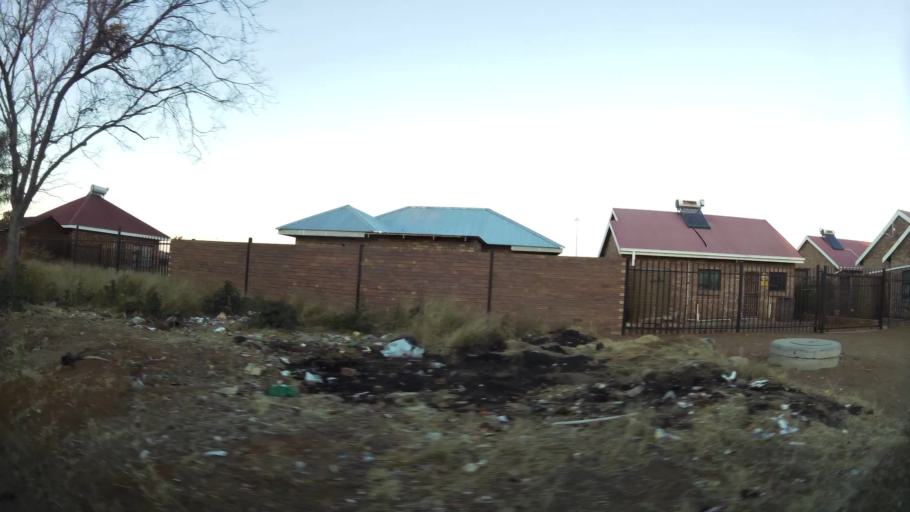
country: ZA
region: Northern Cape
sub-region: Frances Baard District Municipality
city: Kimberley
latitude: -28.7315
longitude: 24.7761
